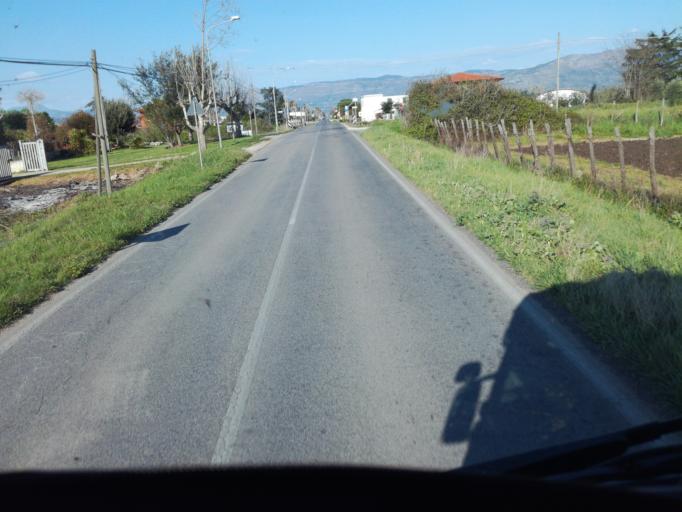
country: IT
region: Latium
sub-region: Provincia di Latina
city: Borgo Hermada
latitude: 41.3750
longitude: 13.1305
